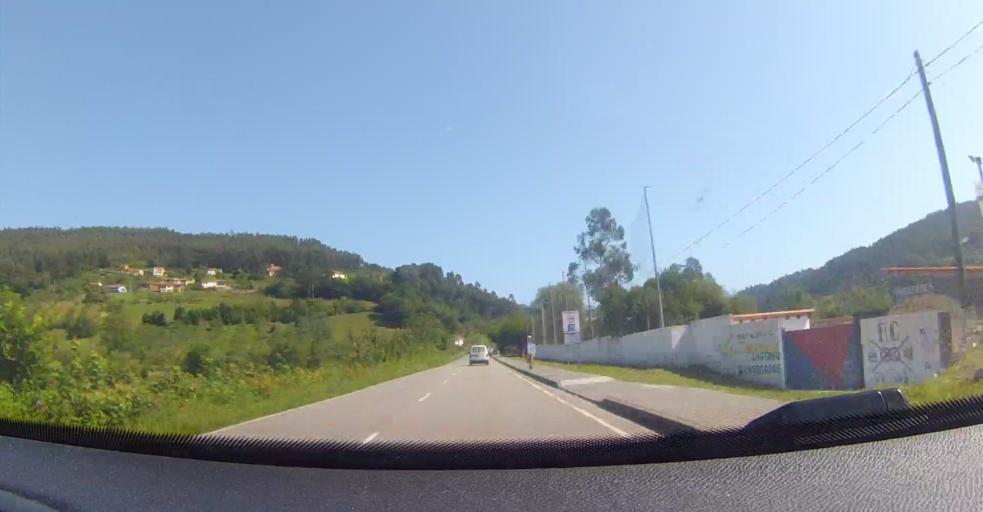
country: ES
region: Asturias
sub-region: Province of Asturias
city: Colunga
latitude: 43.4906
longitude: -5.2682
